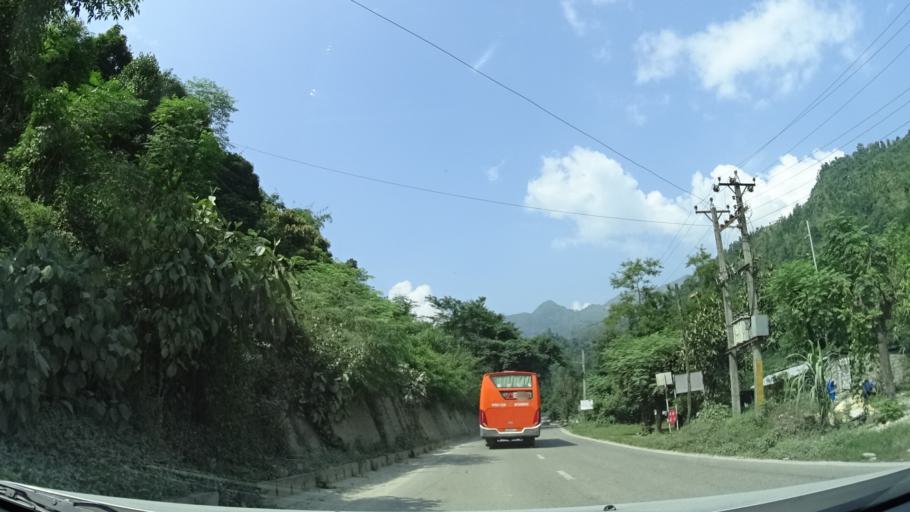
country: NP
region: Central Region
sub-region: Narayani Zone
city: Bharatpur
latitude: 27.8449
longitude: 84.6604
